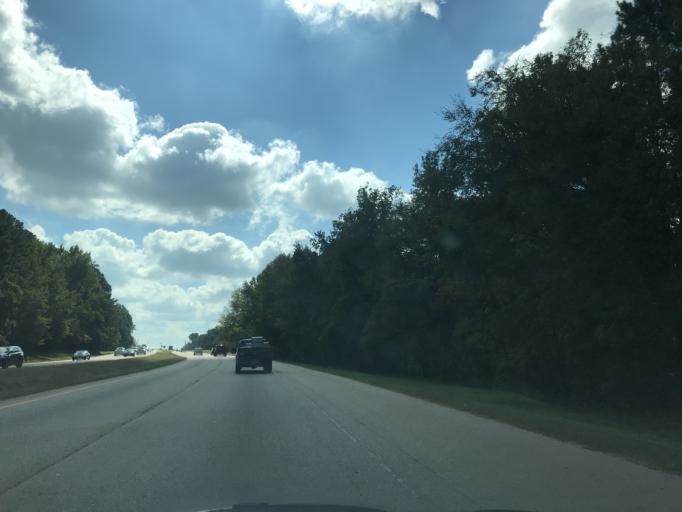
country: US
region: North Carolina
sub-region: Wake County
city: Wake Forest
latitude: 35.9045
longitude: -78.5577
